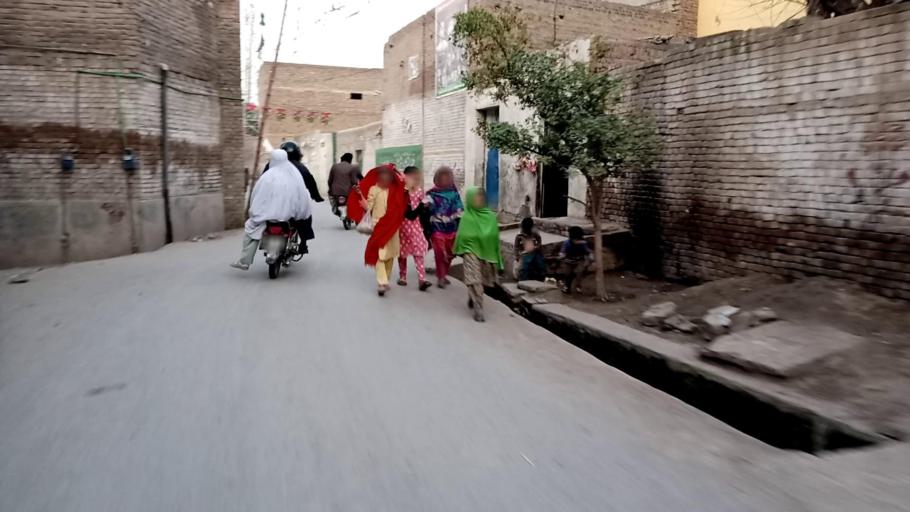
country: PK
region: Khyber Pakhtunkhwa
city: Peshawar
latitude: 34.0292
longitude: 71.4892
